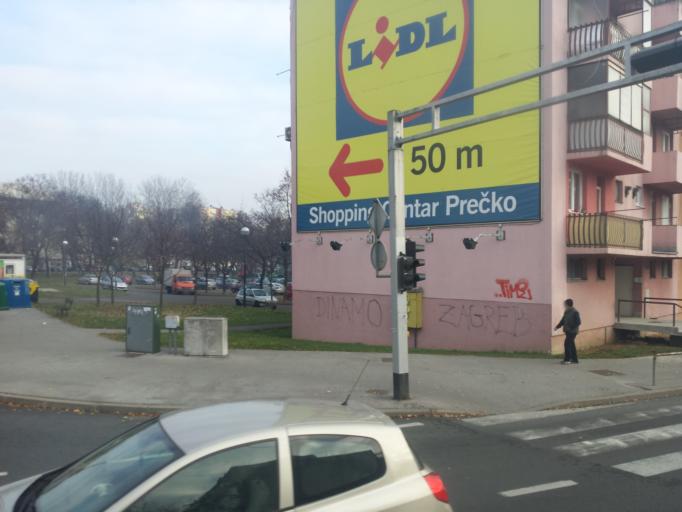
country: HR
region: Grad Zagreb
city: Jankomir
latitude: 45.7942
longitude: 15.8995
